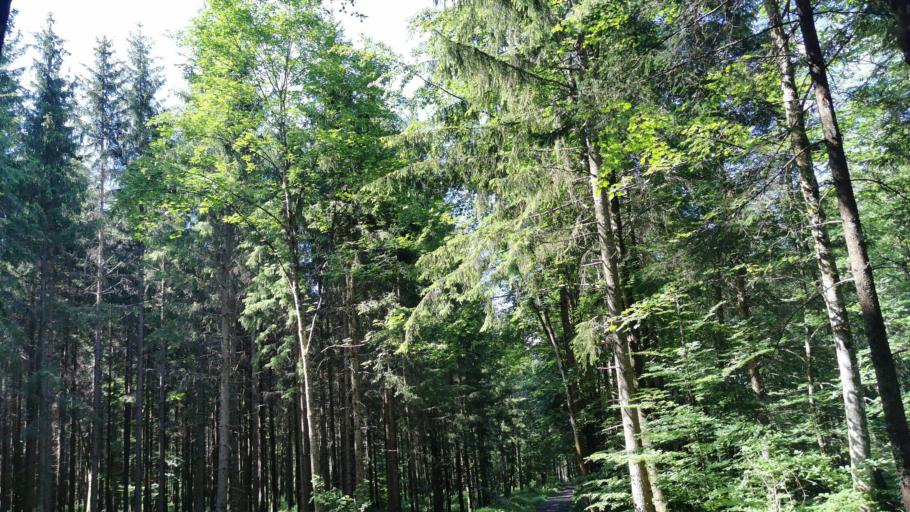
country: DE
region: Bavaria
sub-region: Upper Bavaria
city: Piding
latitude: 47.7427
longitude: 12.9627
